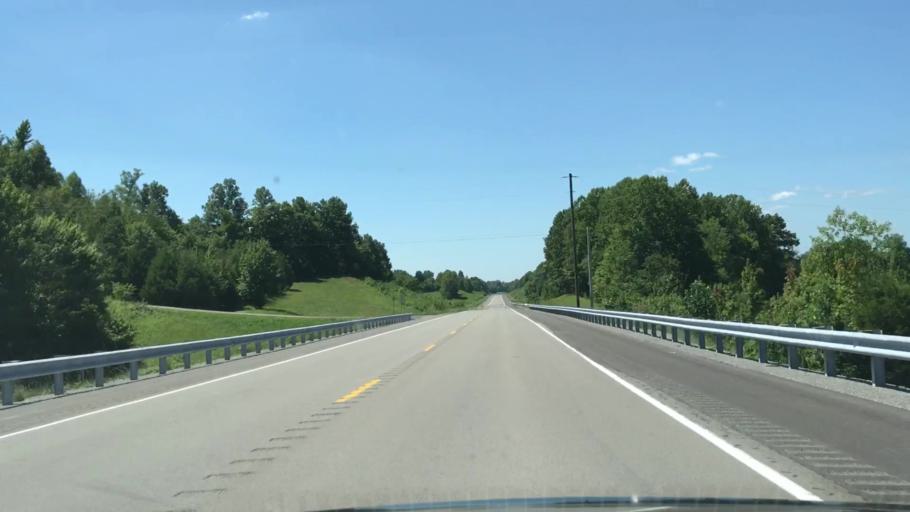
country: US
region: Tennessee
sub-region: Clay County
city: Celina
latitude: 36.6386
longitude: -85.3886
